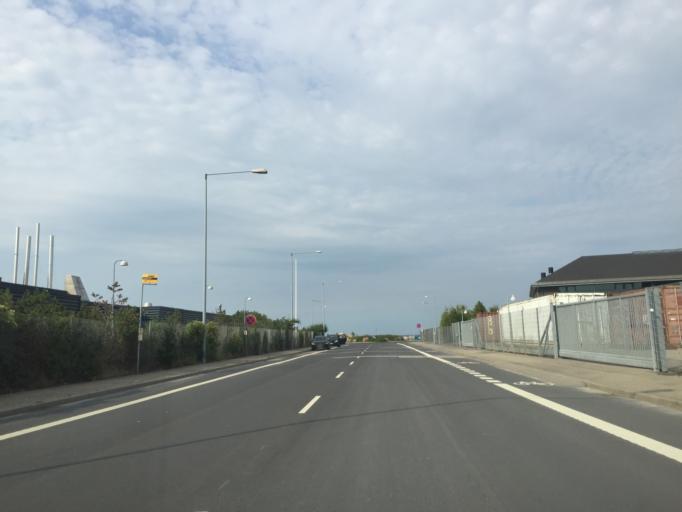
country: DK
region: Capital Region
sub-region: Gentofte Kommune
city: Charlottenlund
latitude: 55.7217
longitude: 12.6088
